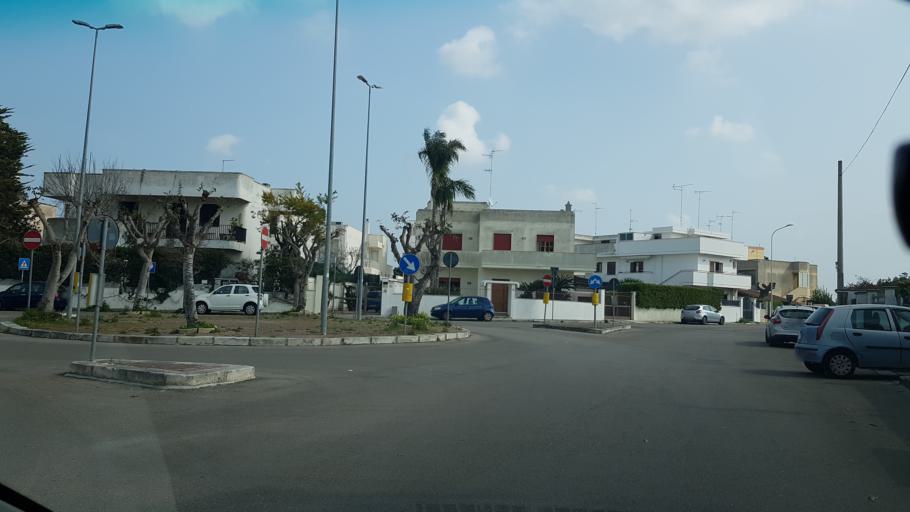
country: IT
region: Apulia
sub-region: Provincia di Lecce
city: Castromediano
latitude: 40.3255
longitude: 18.1776
